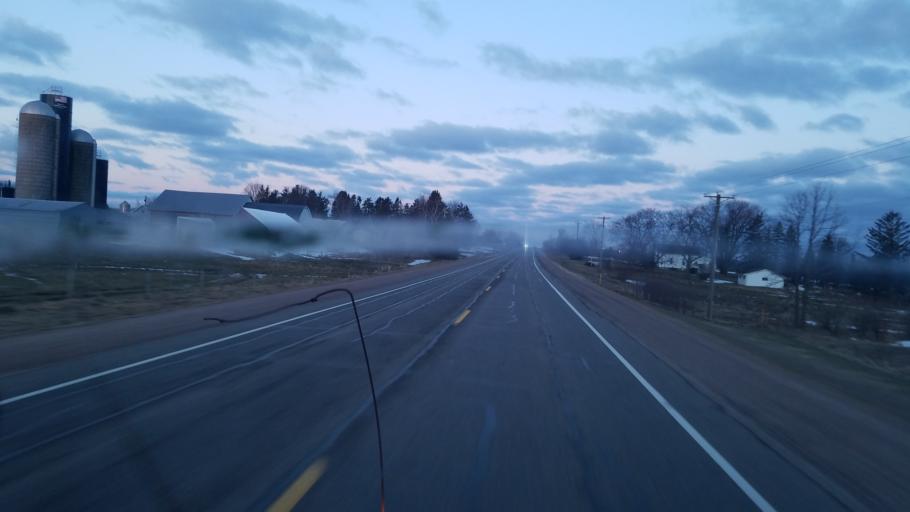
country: US
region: Wisconsin
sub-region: Clark County
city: Loyal
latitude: 44.5819
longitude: -90.4283
